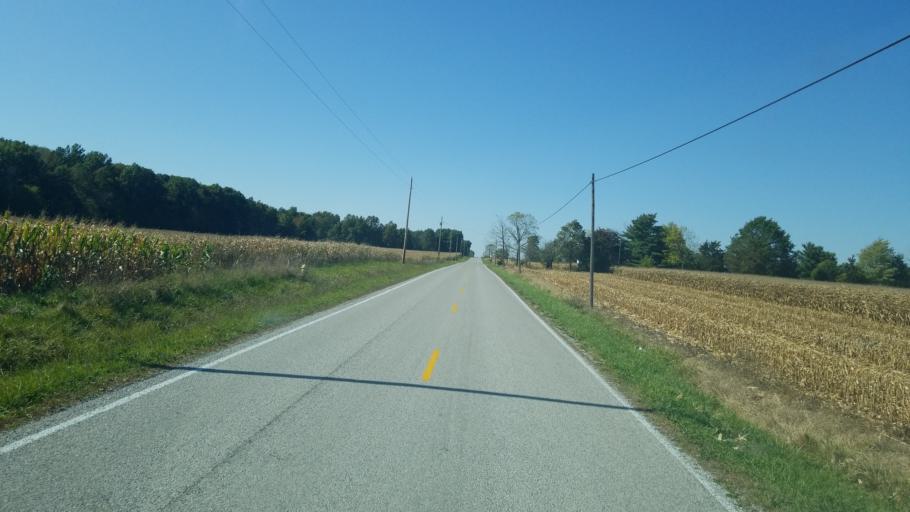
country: US
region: Ohio
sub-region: Huron County
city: Willard
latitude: 41.0326
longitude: -82.7437
